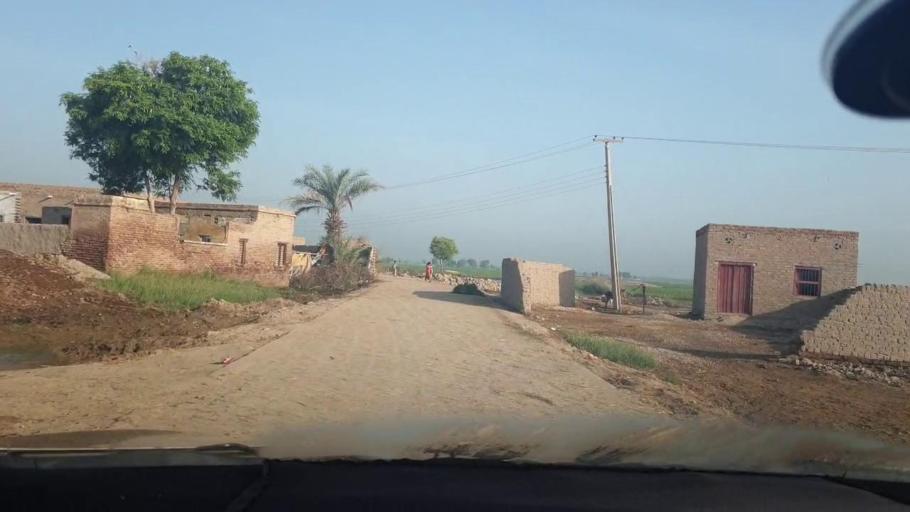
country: PK
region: Sindh
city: Kambar
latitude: 27.6340
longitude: 68.0128
